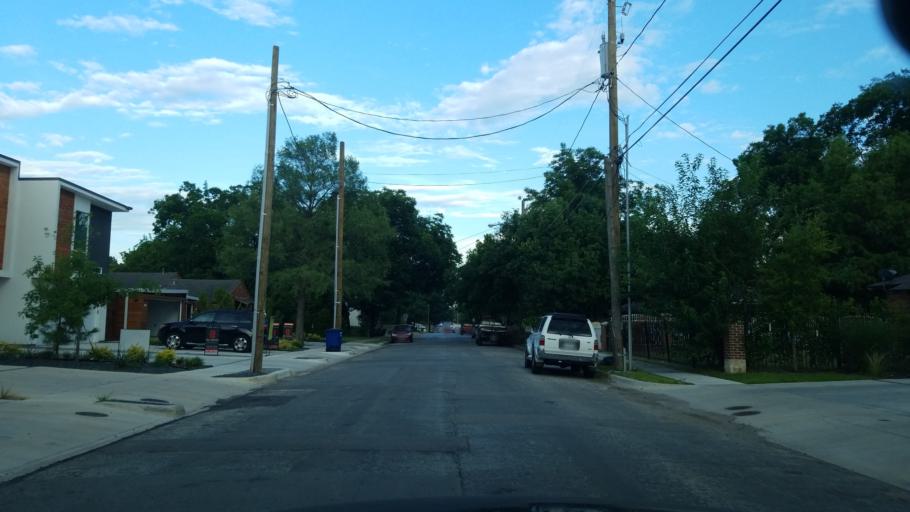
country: US
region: Texas
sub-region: Dallas County
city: Highland Park
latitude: 32.8099
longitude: -96.7823
